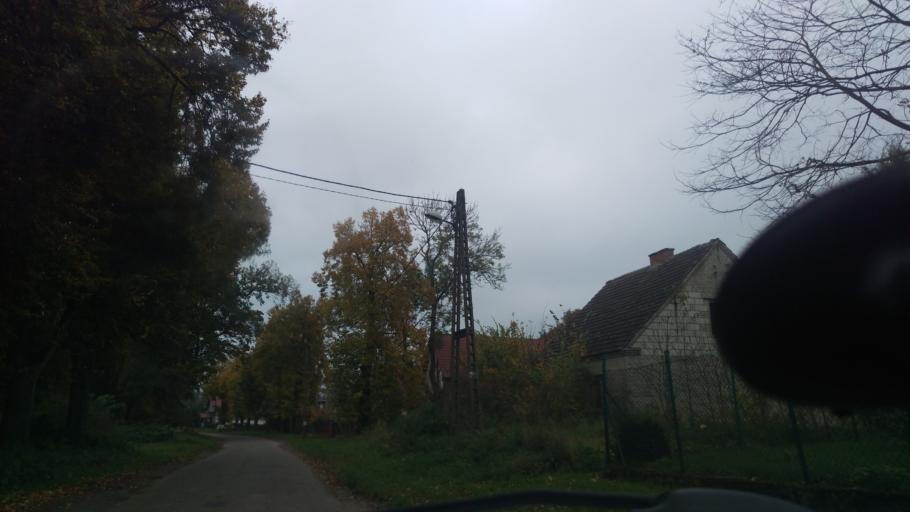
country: PL
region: West Pomeranian Voivodeship
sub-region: Powiat pyrzycki
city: Przelewice
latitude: 53.0500
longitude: 15.1102
